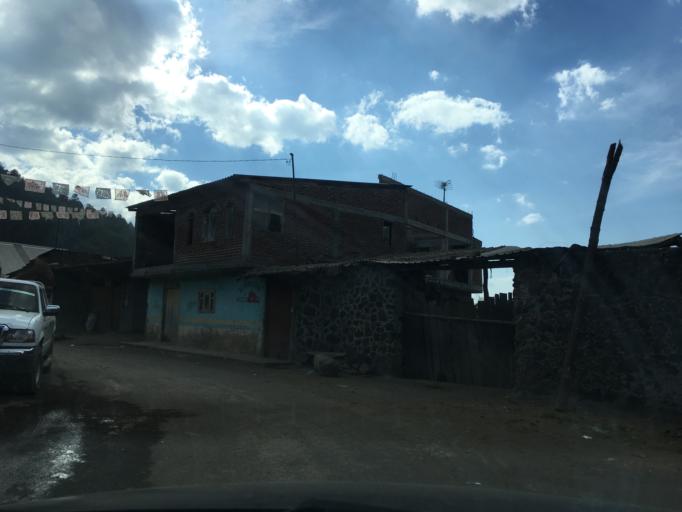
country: MX
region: Michoacan
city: Angahuan
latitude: 19.5471
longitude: -102.2205
